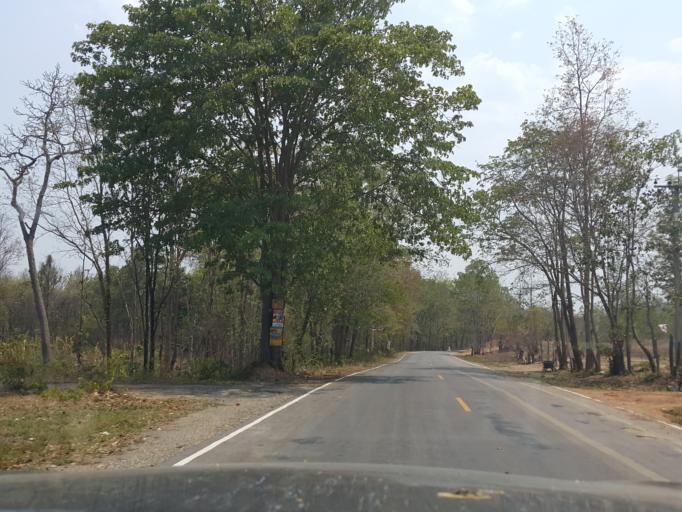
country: TH
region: Lampang
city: Mae Phrik
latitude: 17.4890
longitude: 99.1234
